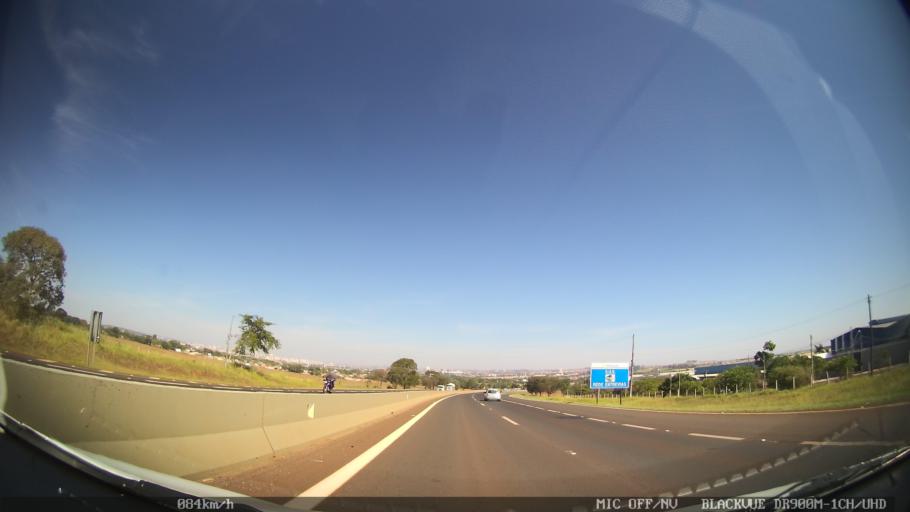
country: BR
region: Sao Paulo
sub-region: Ribeirao Preto
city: Ribeirao Preto
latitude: -21.0975
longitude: -47.7975
